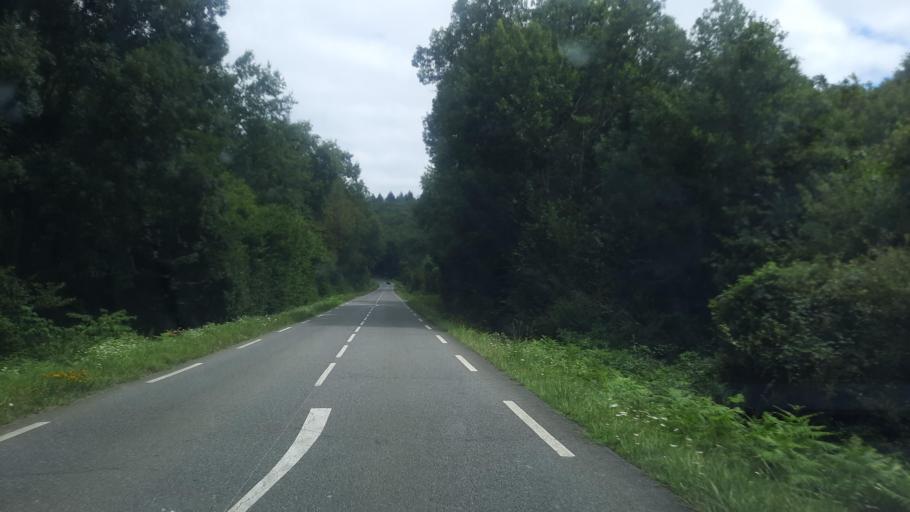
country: FR
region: Midi-Pyrenees
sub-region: Departement des Hautes-Pyrenees
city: Trie-sur-Baise
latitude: 43.2987
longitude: 0.4283
